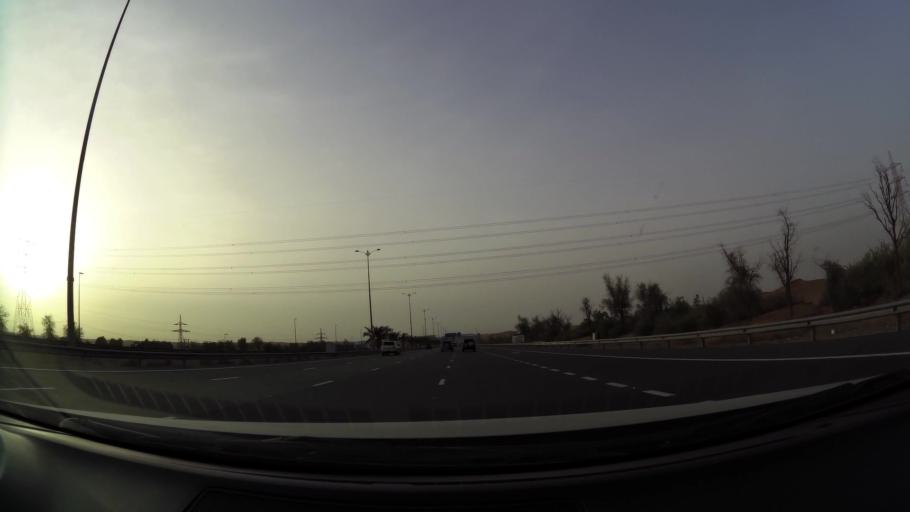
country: OM
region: Al Buraimi
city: Al Buraymi
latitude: 24.3941
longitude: 55.7974
